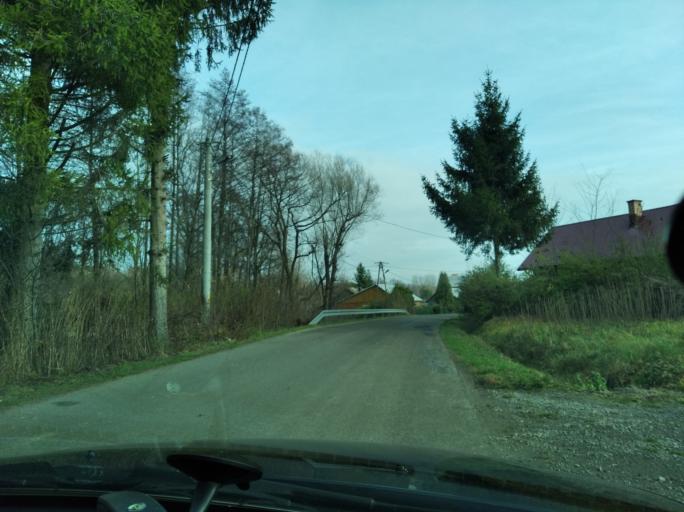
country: PL
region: Subcarpathian Voivodeship
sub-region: Powiat przeworski
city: Siedleczka
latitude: 49.9656
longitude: 22.3697
